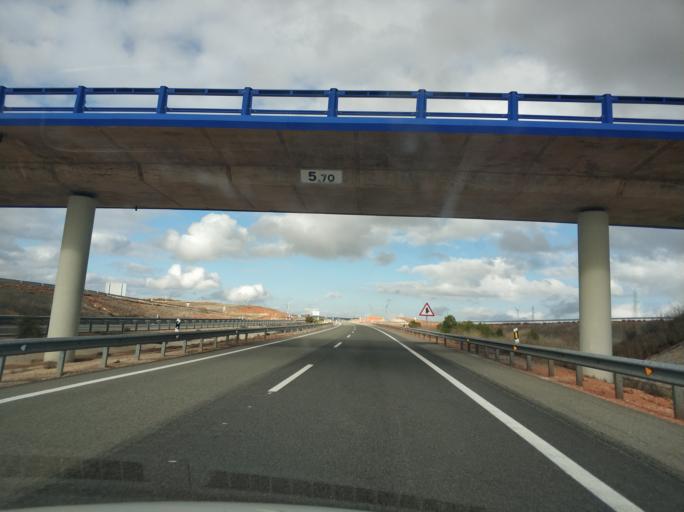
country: ES
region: Castille and Leon
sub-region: Provincia de Soria
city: Alcubilla de las Penas
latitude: 41.2607
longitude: -2.4732
